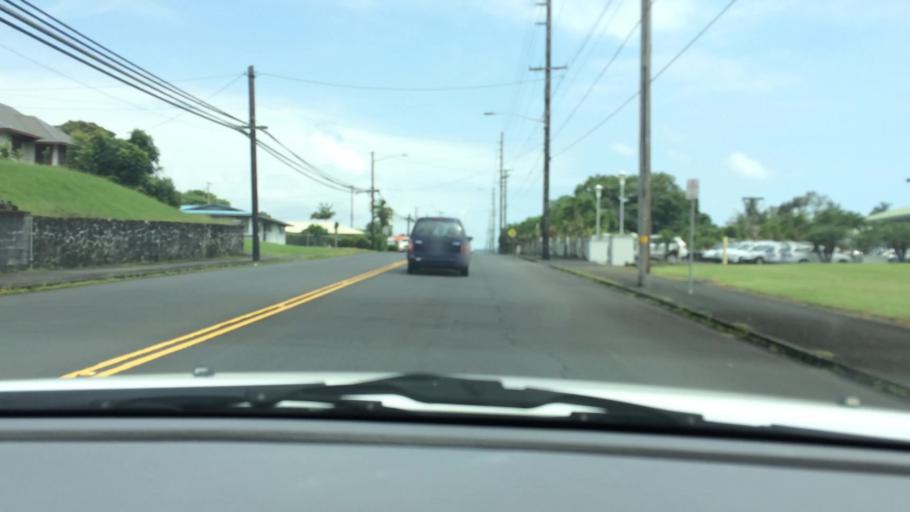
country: US
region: Hawaii
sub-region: Hawaii County
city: Hilo
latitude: 19.7127
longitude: -155.0811
